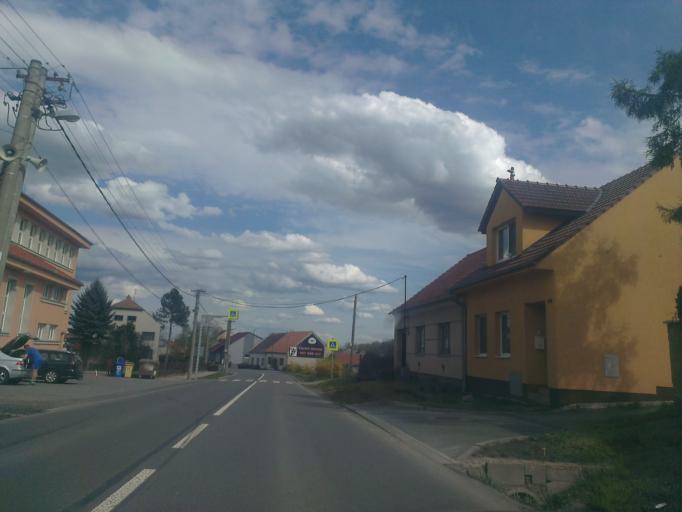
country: CZ
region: South Moravian
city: Zelesice
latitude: 49.1153
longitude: 16.5732
